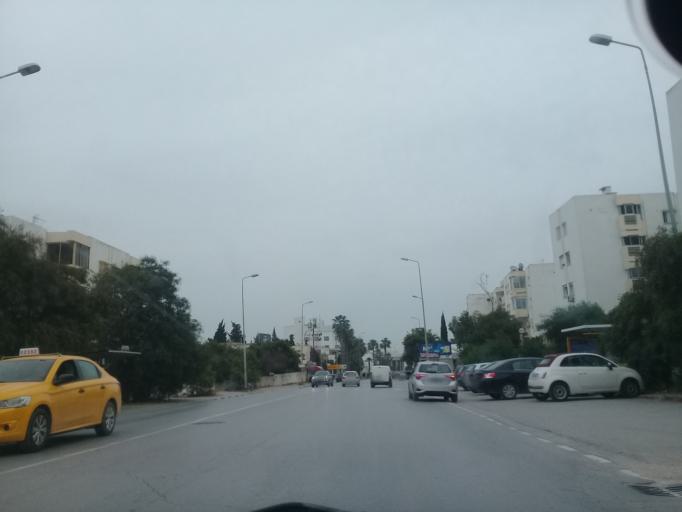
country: TN
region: Tunis
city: Tunis
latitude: 36.8483
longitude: 10.1516
